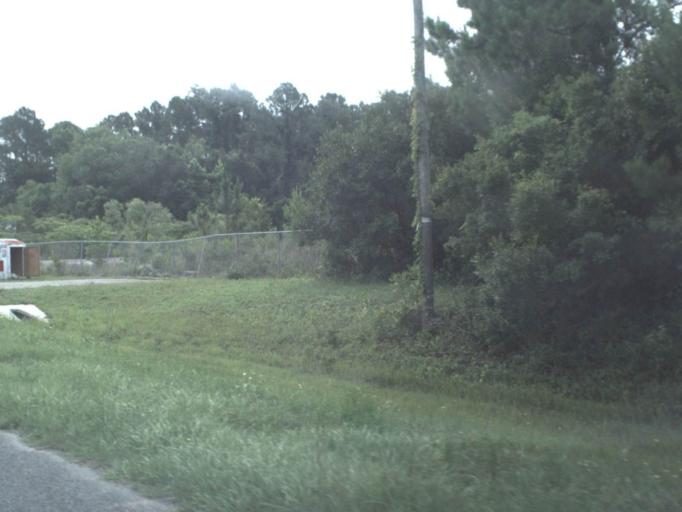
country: US
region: Florida
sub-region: Nassau County
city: Yulee
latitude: 30.6179
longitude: -81.6548
